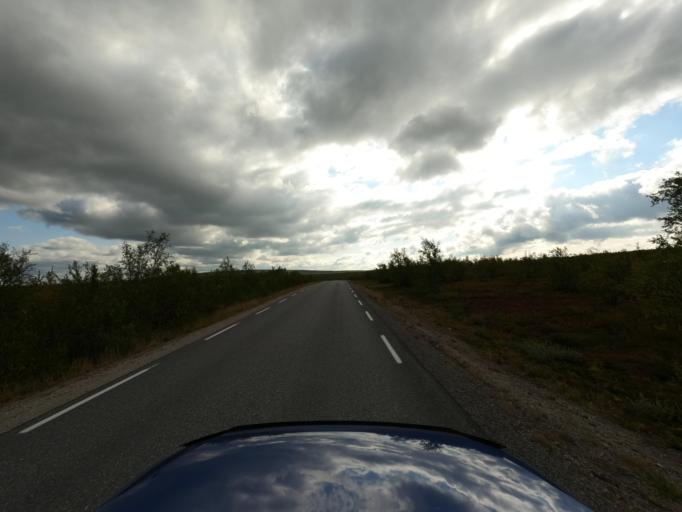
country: NO
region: Finnmark Fylke
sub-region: Porsanger
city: Lakselv
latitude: 69.3700
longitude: 24.2800
